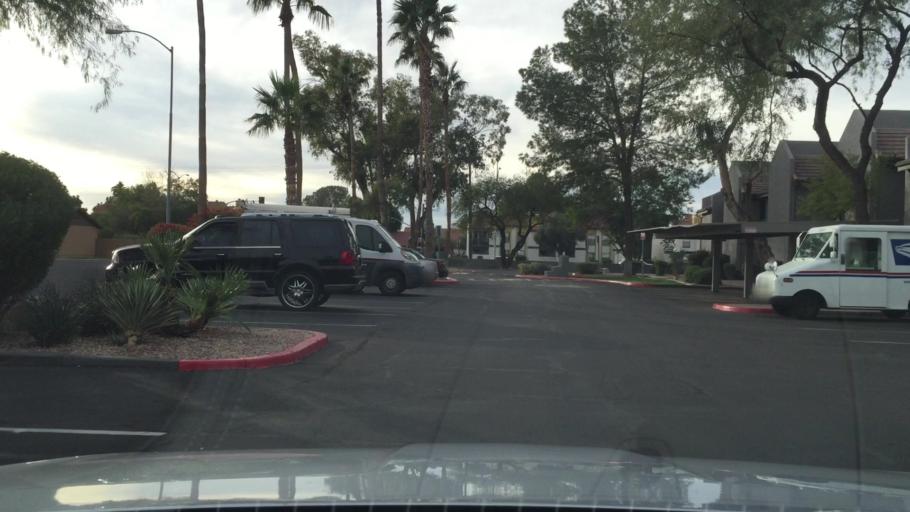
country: US
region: Arizona
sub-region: Maricopa County
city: Gilbert
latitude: 33.3845
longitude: -111.7871
